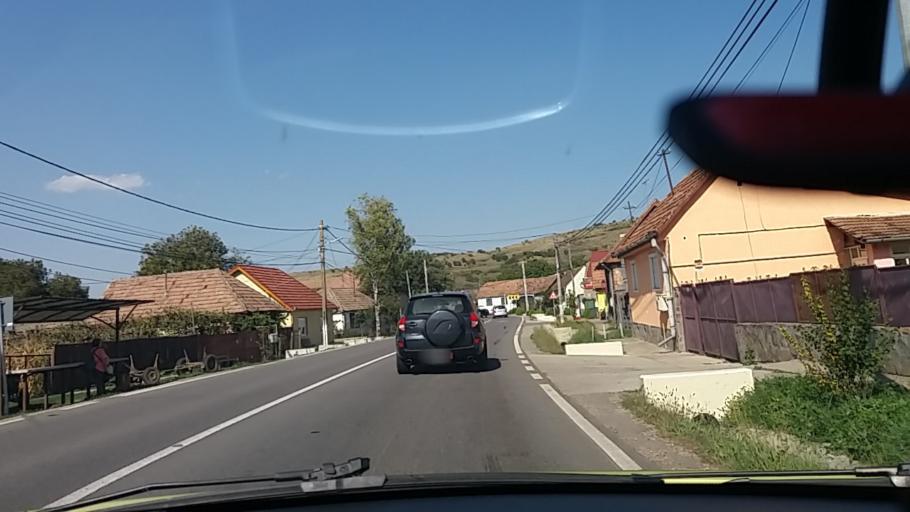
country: RO
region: Sibiu
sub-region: Comuna Slimnic
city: Slimnic
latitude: 45.9620
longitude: 24.1632
